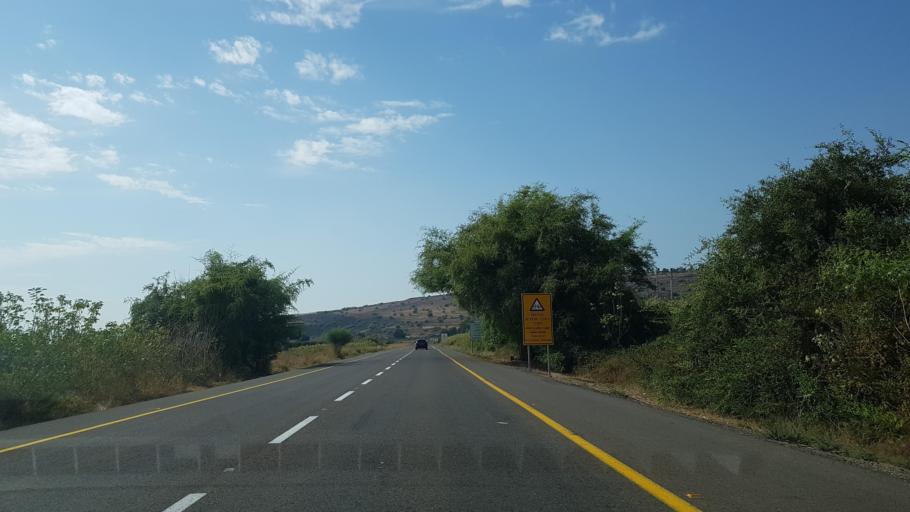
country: SY
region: Quneitra
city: Al Butayhah
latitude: 32.9041
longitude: 35.6287
